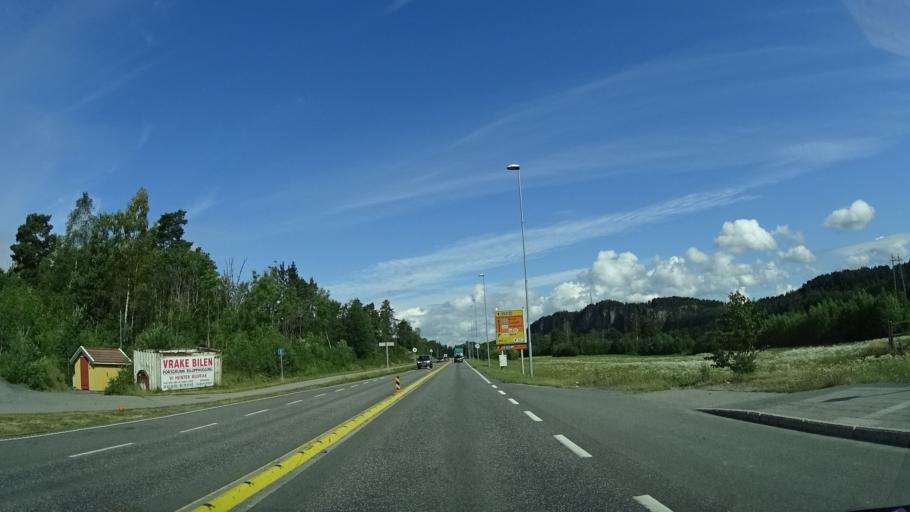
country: NO
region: Telemark
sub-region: Bamble
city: Langesund
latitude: 59.0297
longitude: 9.6794
